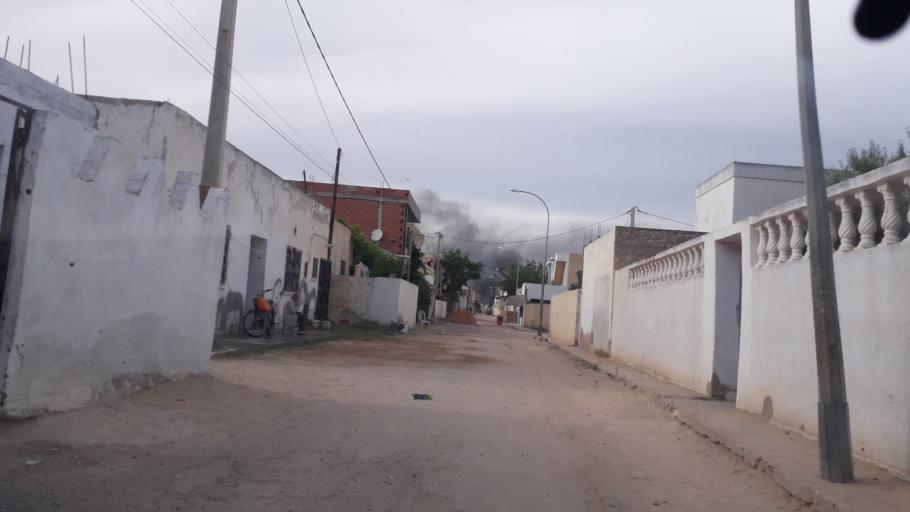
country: TN
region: Safaqis
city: Al Qarmadah
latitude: 34.8844
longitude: 10.7595
